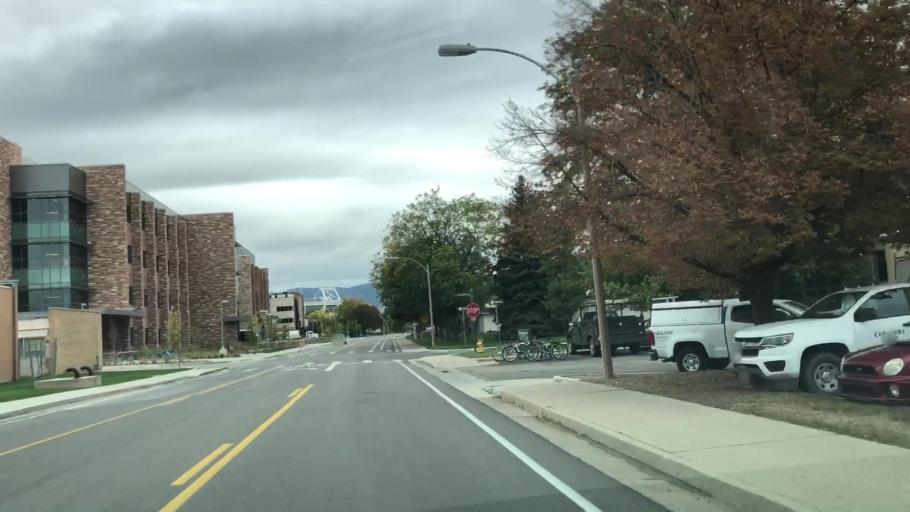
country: US
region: Colorado
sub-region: Larimer County
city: Fort Collins
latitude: 40.5708
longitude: -105.0796
